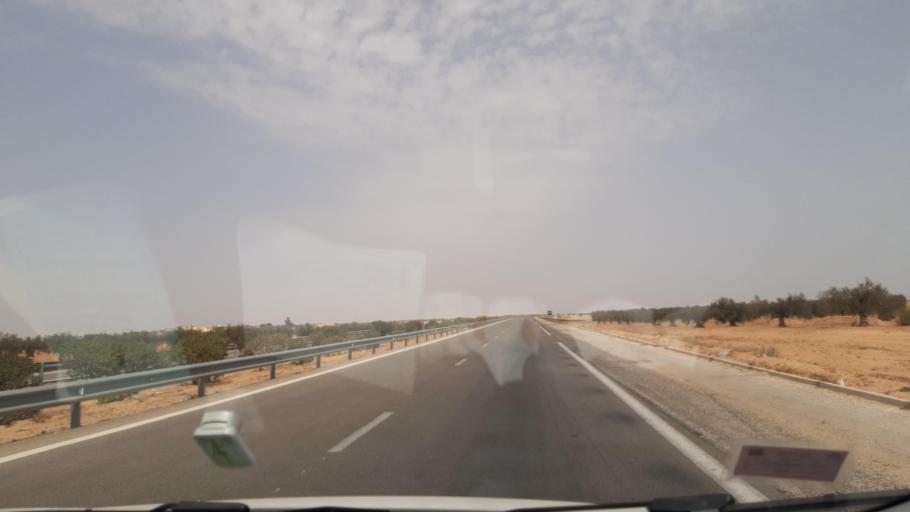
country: TN
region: Safaqis
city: Bi'r `Ali Bin Khalifah
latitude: 34.5614
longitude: 10.3411
